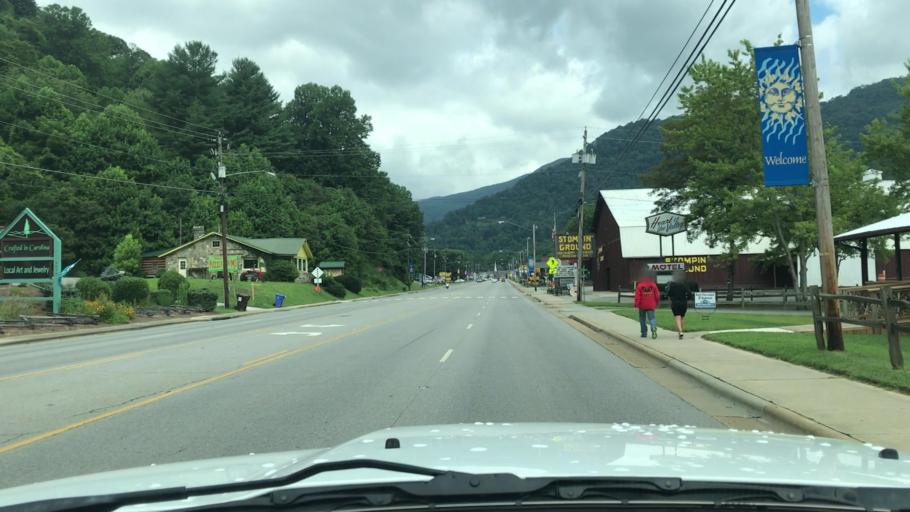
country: US
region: North Carolina
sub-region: Haywood County
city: Maggie Valley
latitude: 35.5134
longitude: -83.0799
